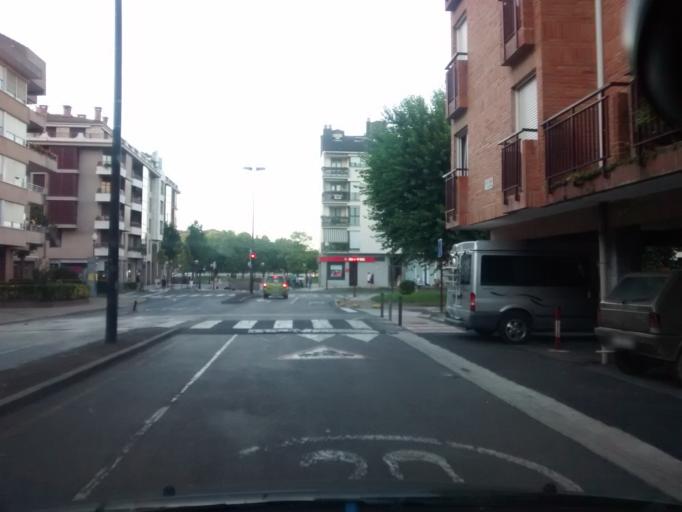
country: ES
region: Basque Country
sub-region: Provincia de Guipuzcoa
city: Zumaia
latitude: 43.2937
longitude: -2.2561
